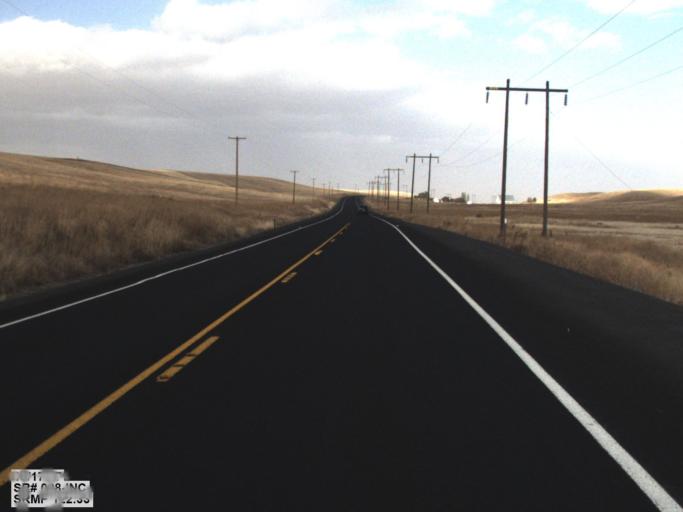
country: US
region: Washington
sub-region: Lincoln County
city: Davenport
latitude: 47.5334
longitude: -118.1992
